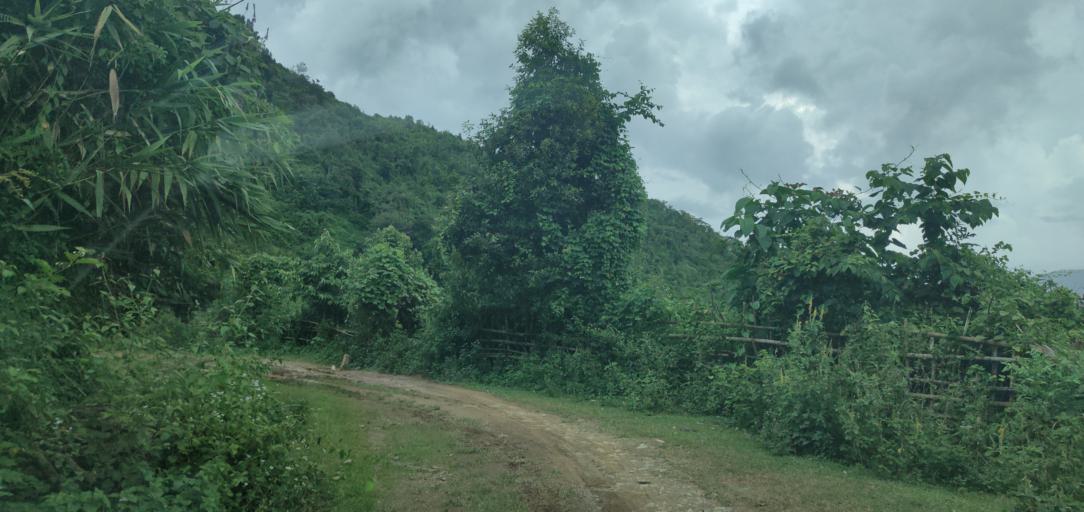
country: LA
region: Phongsali
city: Phongsali
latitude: 21.4405
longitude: 102.3248
